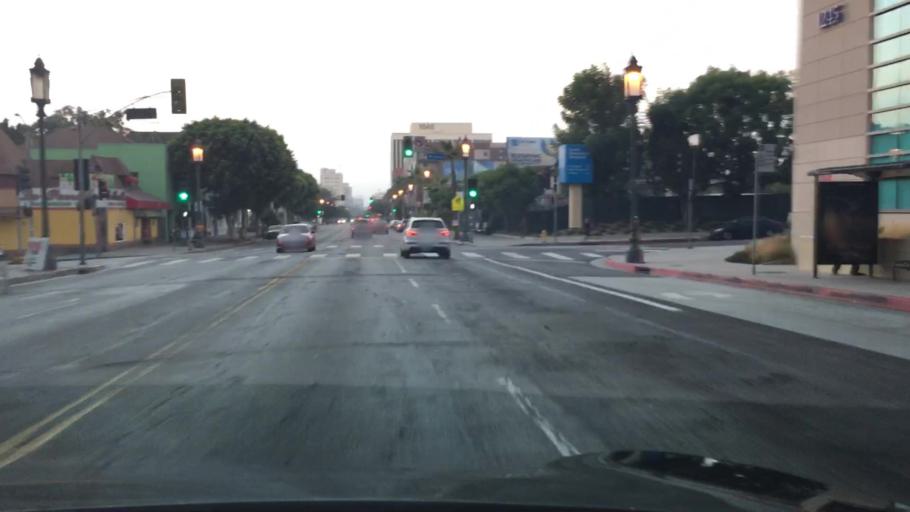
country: US
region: California
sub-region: Los Angeles County
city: Los Angeles
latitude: 34.0540
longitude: -118.2670
